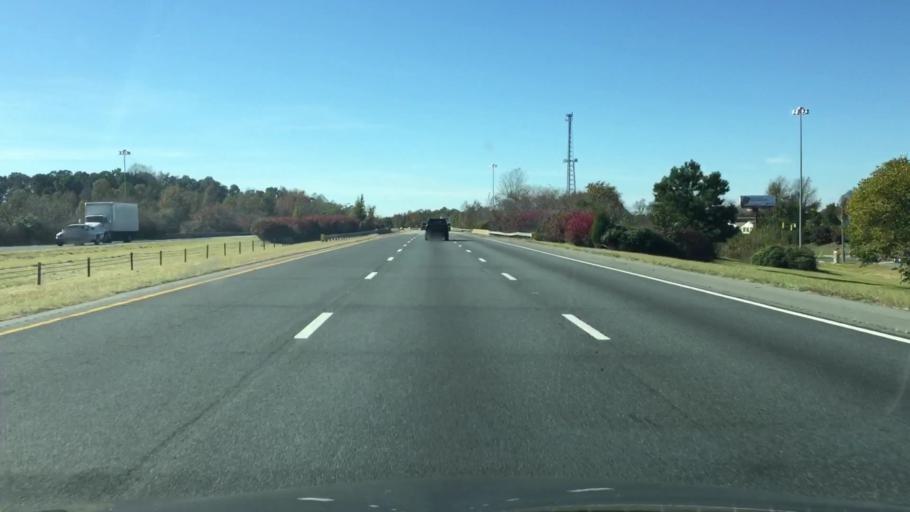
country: US
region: North Carolina
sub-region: Davidson County
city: Thomasville
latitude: 35.8602
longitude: -80.0709
